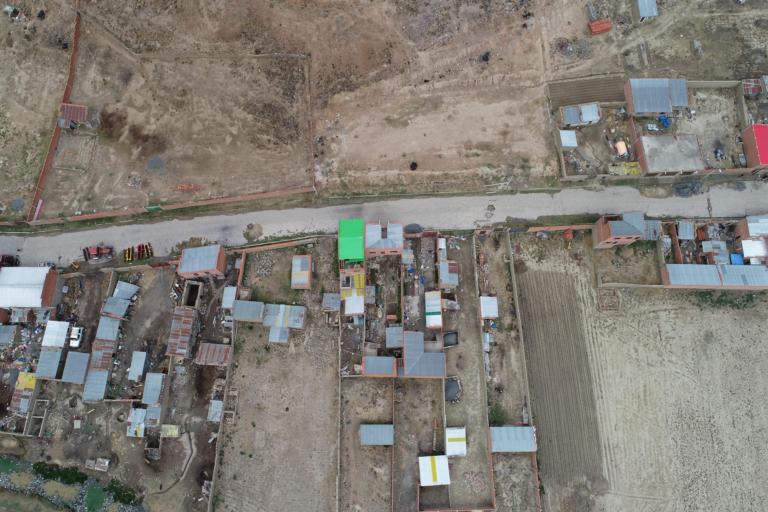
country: BO
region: La Paz
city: Achacachi
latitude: -16.0518
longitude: -68.6835
